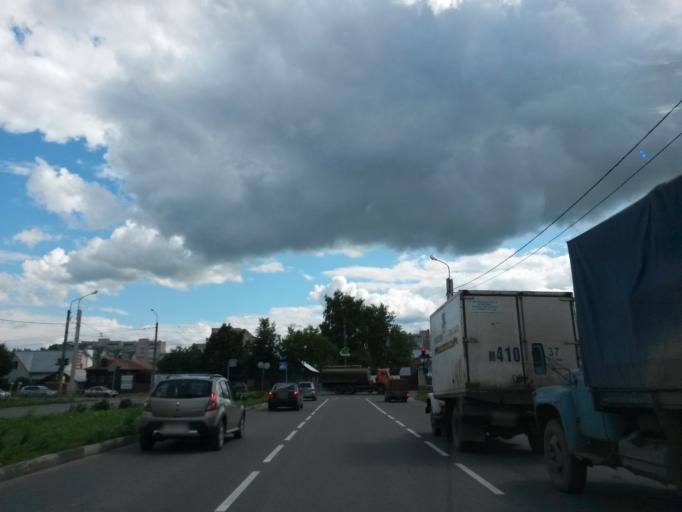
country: RU
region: Ivanovo
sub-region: Gorod Ivanovo
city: Ivanovo
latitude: 56.9933
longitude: 40.9664
